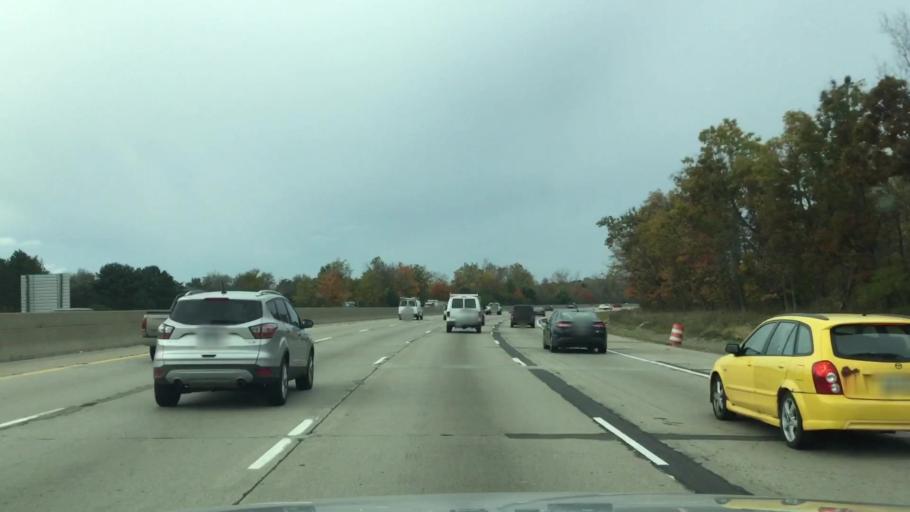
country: US
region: Michigan
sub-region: Oakland County
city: Franklin
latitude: 42.4909
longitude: -83.3291
